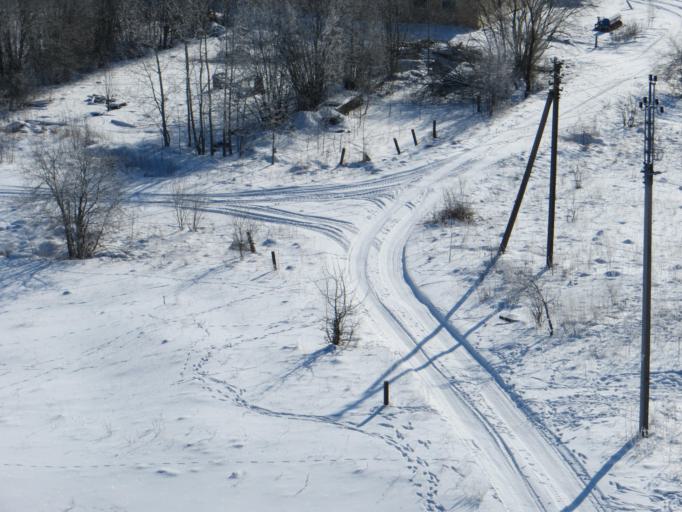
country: LT
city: Zarasai
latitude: 55.7729
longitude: 25.9950
